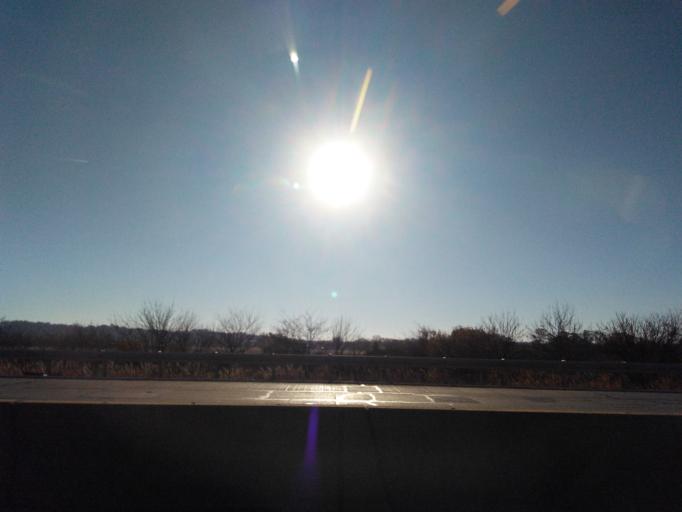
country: US
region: Illinois
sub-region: Saint Clair County
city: Washington Park
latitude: 38.6149
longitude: -90.0715
